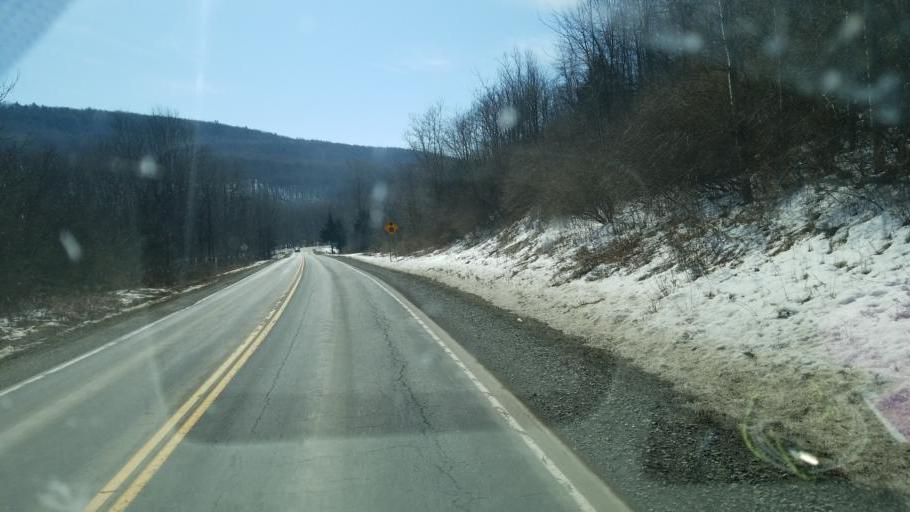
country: US
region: New York
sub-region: Steuben County
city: Hornell
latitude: 42.3414
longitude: -77.7224
